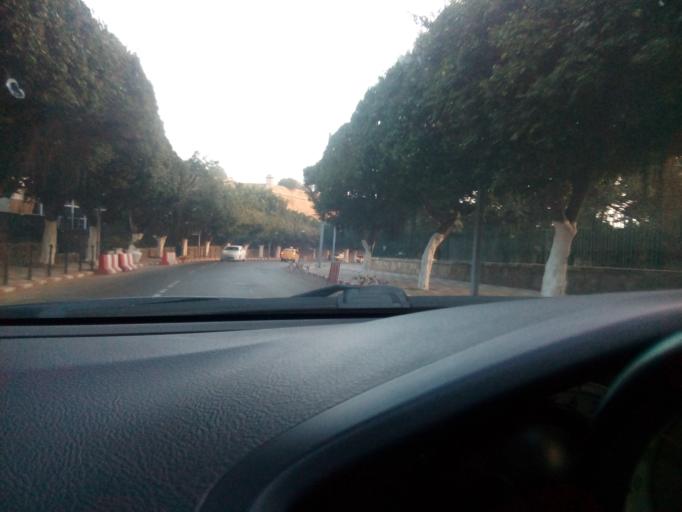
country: DZ
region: Oran
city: Oran
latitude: 35.7058
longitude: -0.6471
